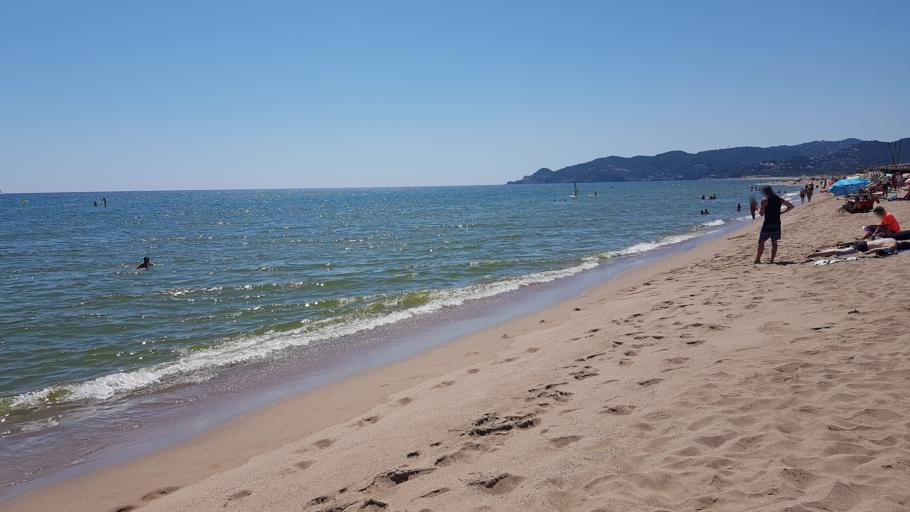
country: ES
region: Catalonia
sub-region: Provincia de Girona
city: Pals
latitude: 42.0097
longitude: 3.1961
